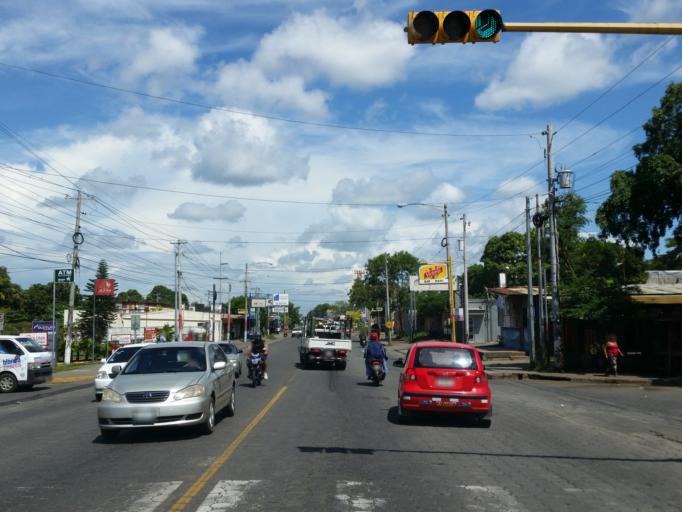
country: NI
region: Managua
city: Managua
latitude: 12.1293
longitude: -86.2248
